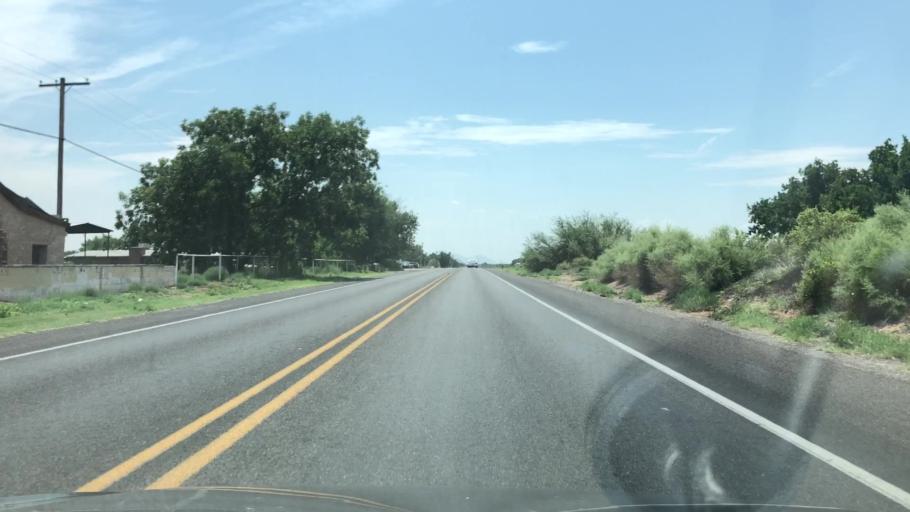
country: US
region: New Mexico
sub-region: Dona Ana County
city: Mesquite
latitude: 32.2013
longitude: -106.7198
